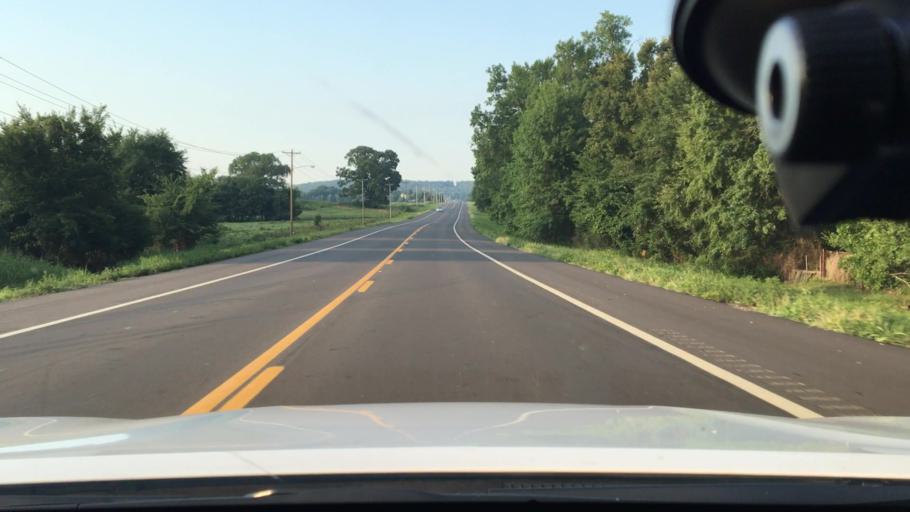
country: US
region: Arkansas
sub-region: Johnson County
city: Clarksville
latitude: 35.4458
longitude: -93.5291
